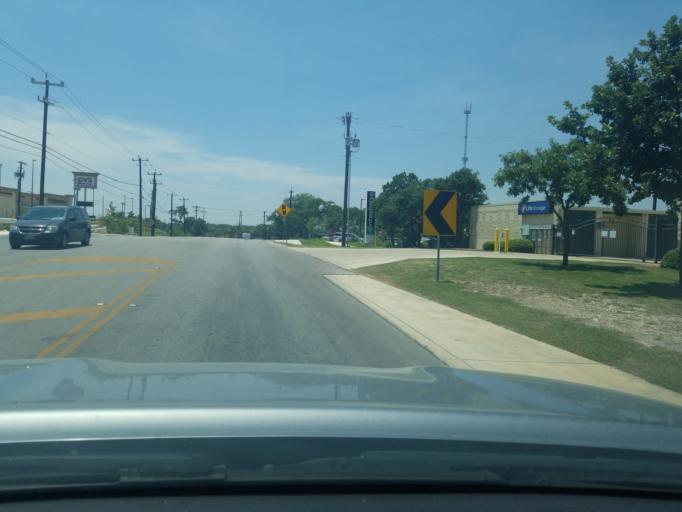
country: US
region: Texas
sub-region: Bexar County
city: Timberwood Park
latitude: 29.6612
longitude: -98.4478
